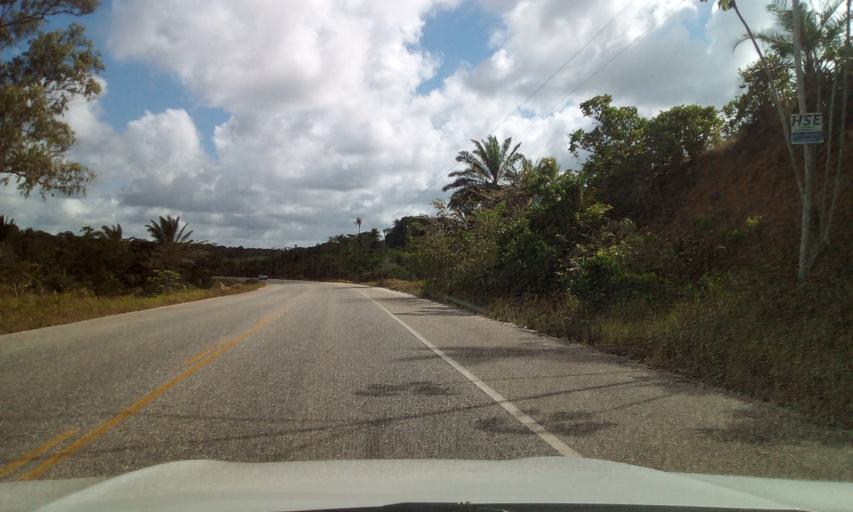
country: BR
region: Sergipe
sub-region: Estancia
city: Estancia
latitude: -11.3852
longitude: -37.4672
